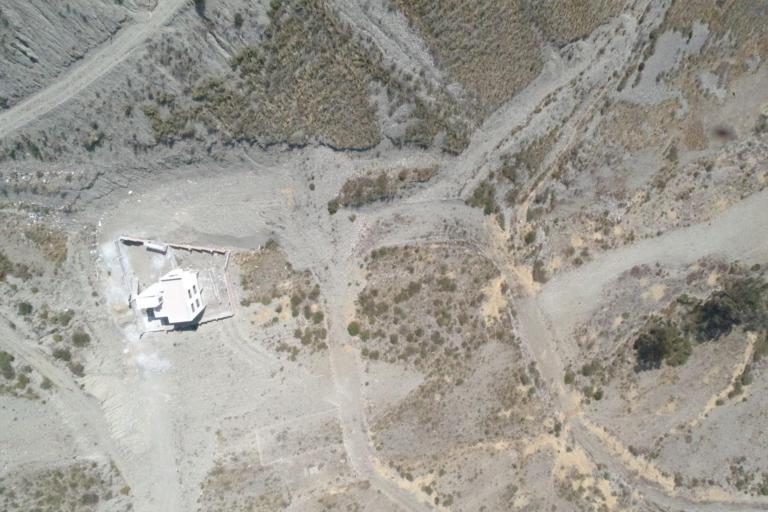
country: BO
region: La Paz
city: La Paz
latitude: -16.4743
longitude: -68.0972
